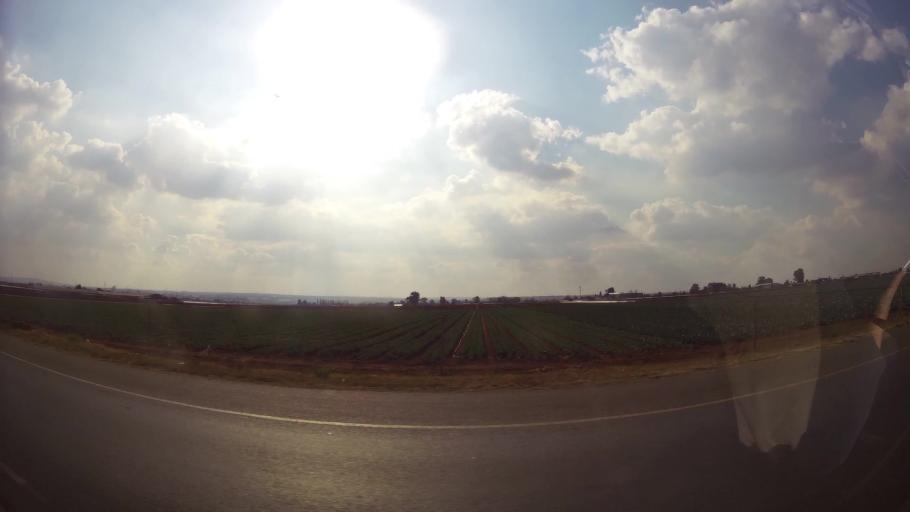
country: ZA
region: Gauteng
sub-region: Ekurhuleni Metropolitan Municipality
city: Germiston
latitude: -26.2911
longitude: 28.2246
